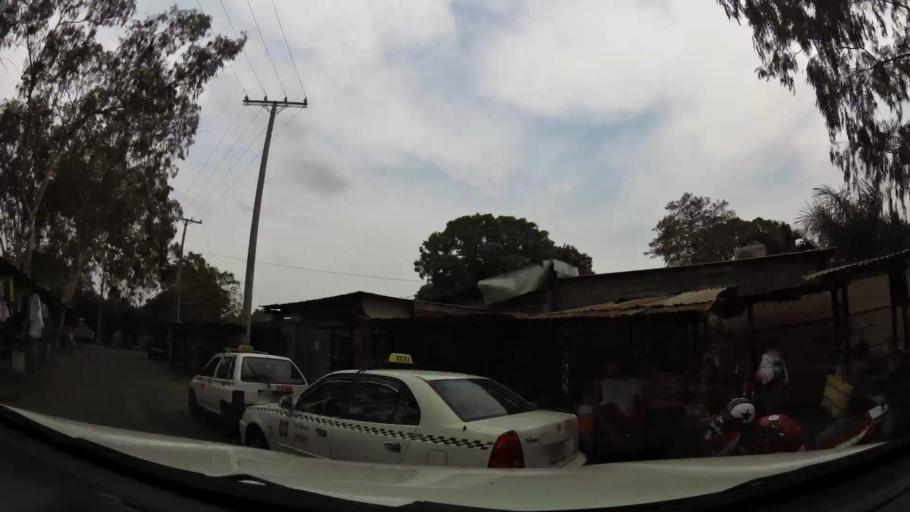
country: NI
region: Managua
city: Managua
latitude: 12.1234
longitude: -86.2370
